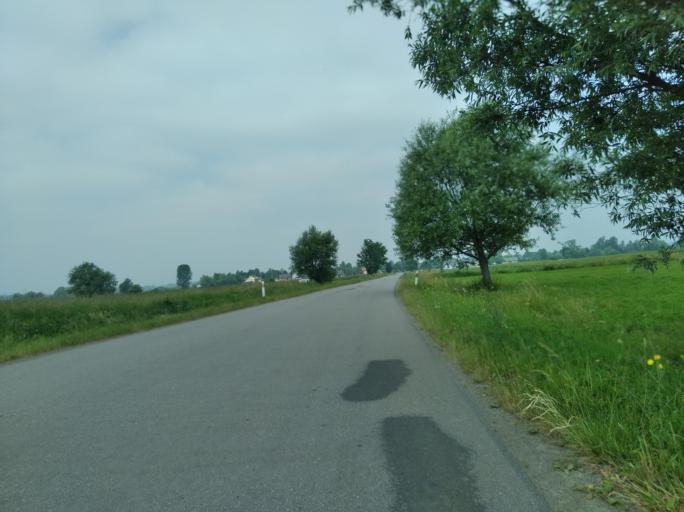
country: PL
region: Subcarpathian Voivodeship
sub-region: Powiat sanocki
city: Besko
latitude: 49.6126
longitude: 21.9511
